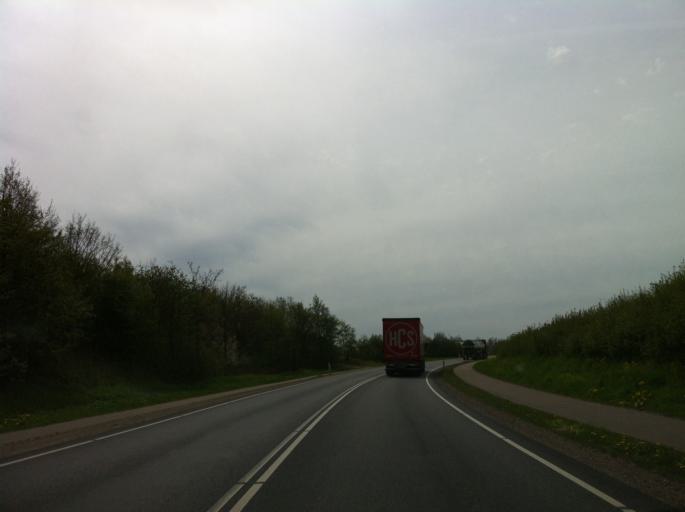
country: DK
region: Zealand
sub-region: Ringsted Kommune
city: Ringsted
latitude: 55.4398
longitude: 11.8255
